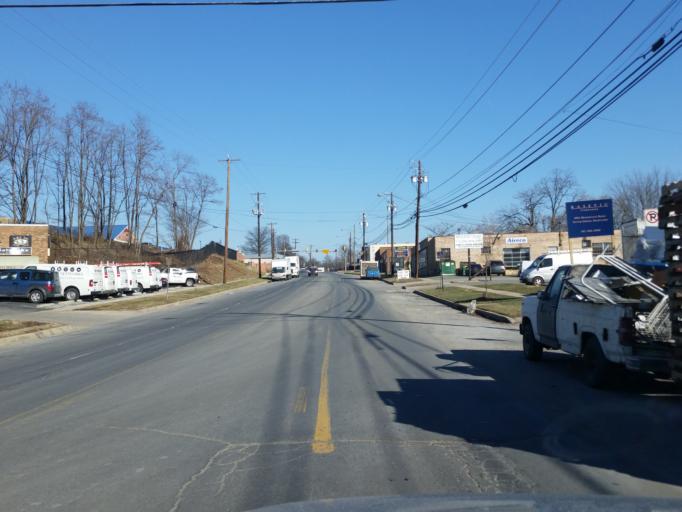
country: US
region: Maryland
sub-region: Montgomery County
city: Forest Glen
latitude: 39.0014
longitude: -77.0539
